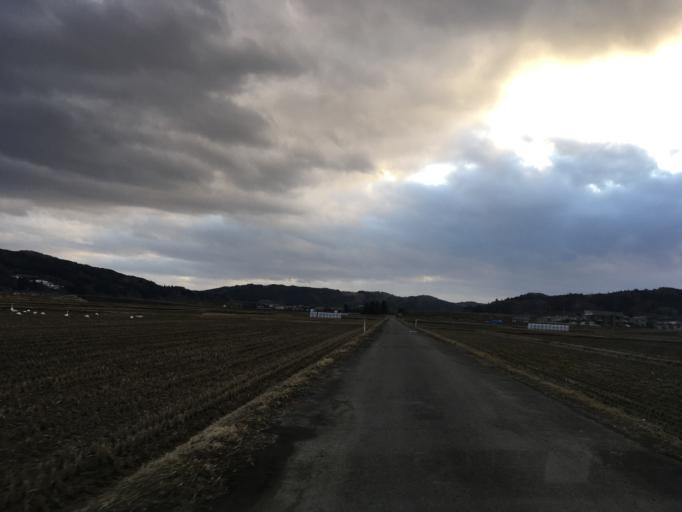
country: JP
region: Iwate
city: Ichinoseki
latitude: 38.8460
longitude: 141.2707
